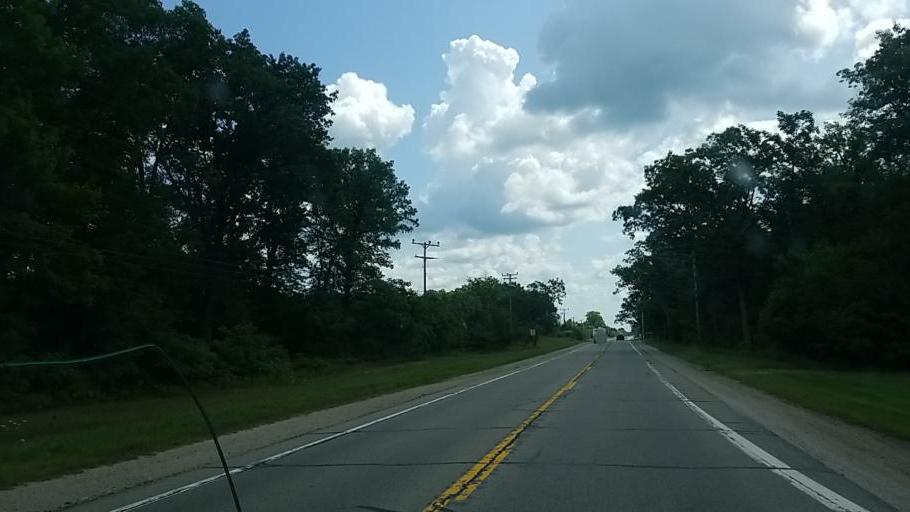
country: US
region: Michigan
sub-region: Muskegon County
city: Wolf Lake
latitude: 43.2351
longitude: -86.0524
